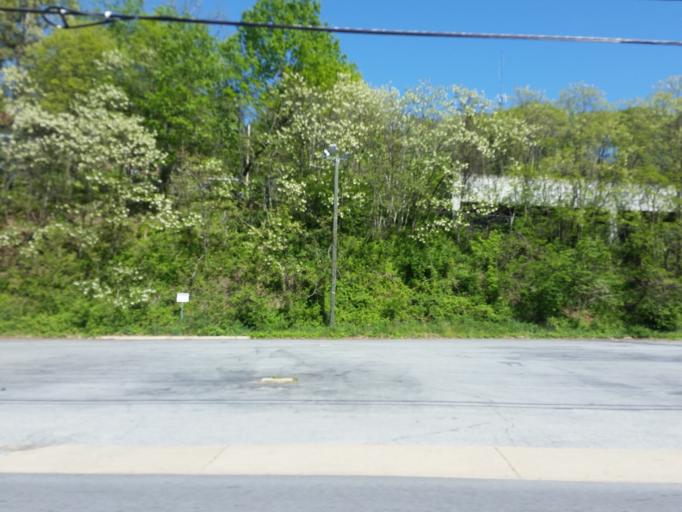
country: US
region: North Carolina
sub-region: Buncombe County
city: Asheville
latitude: 35.5841
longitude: -82.5513
